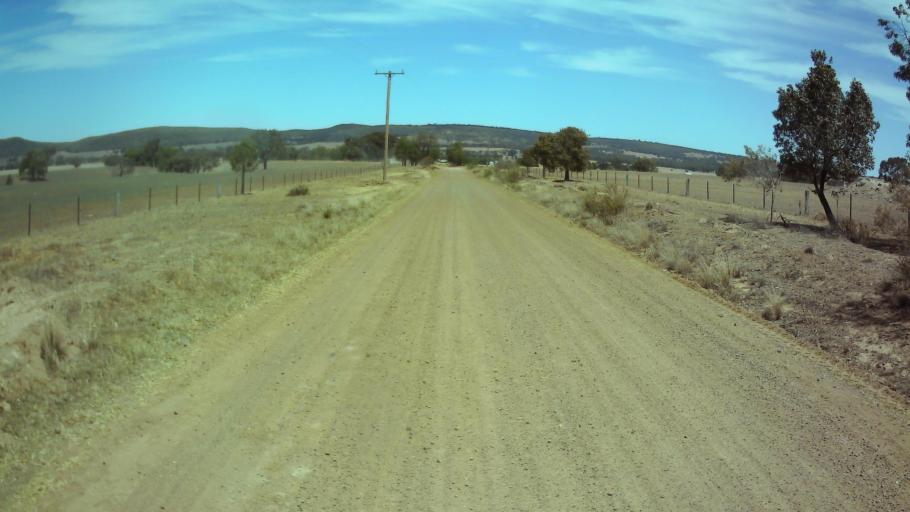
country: AU
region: New South Wales
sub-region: Weddin
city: Grenfell
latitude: -33.8244
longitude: 148.1698
